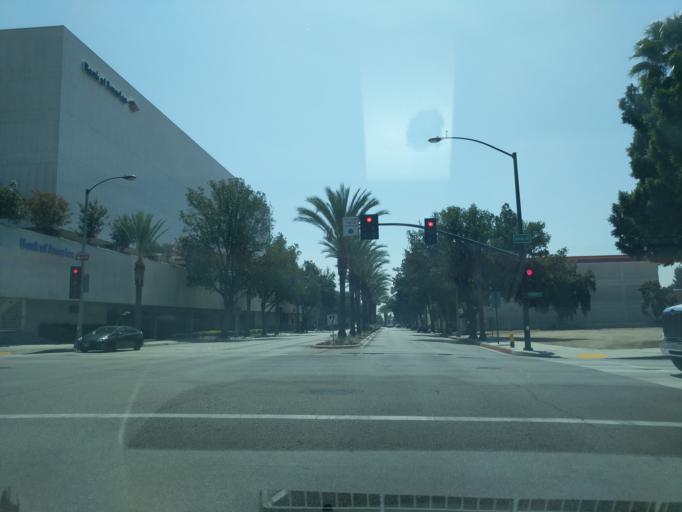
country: US
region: California
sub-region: Los Angeles County
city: Pasadena
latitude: 34.1447
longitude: -118.1475
